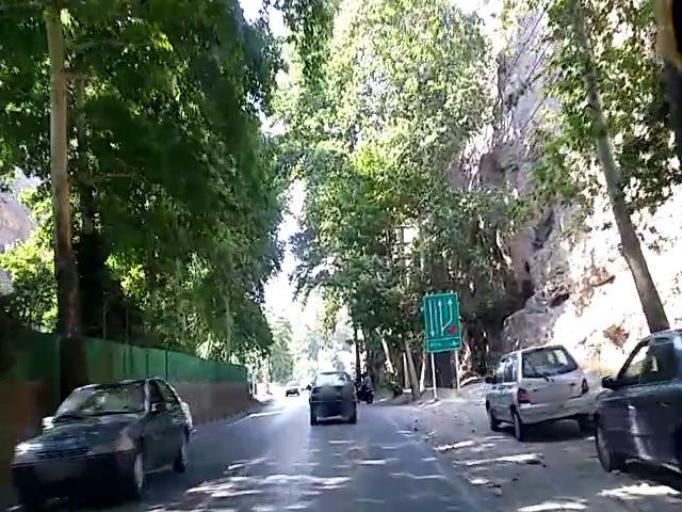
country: IR
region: Alborz
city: Karaj
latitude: 35.8938
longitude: 51.0458
